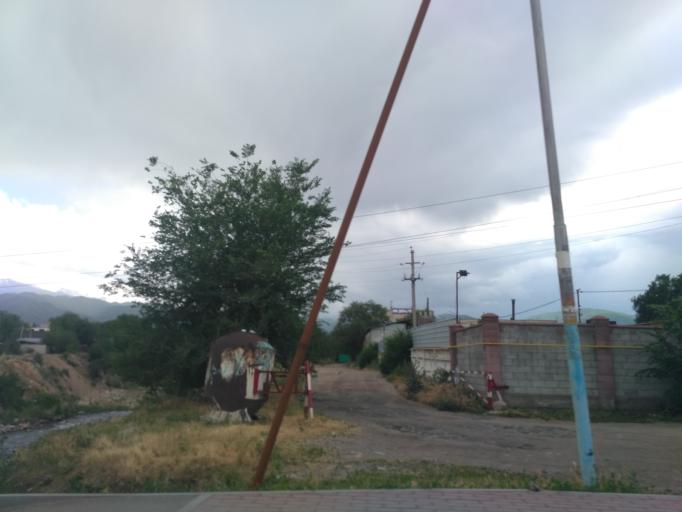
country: KZ
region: Almaty Oblysy
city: Burunday
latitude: 43.2086
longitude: 76.6349
